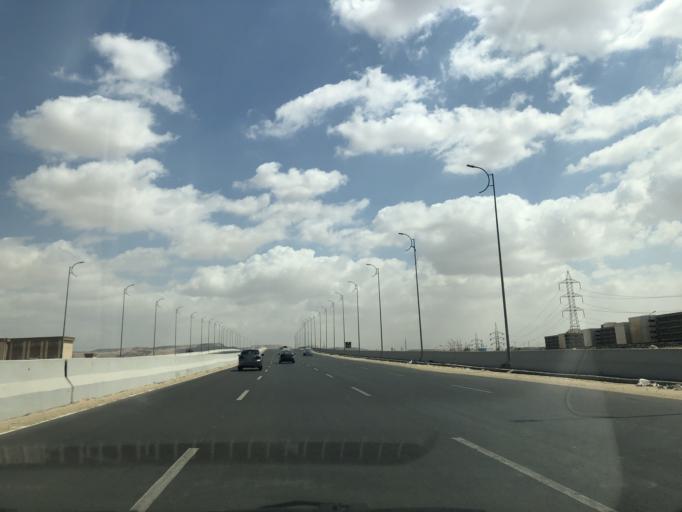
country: EG
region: Muhafazat al Qahirah
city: Halwan
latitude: 29.8718
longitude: 31.3102
